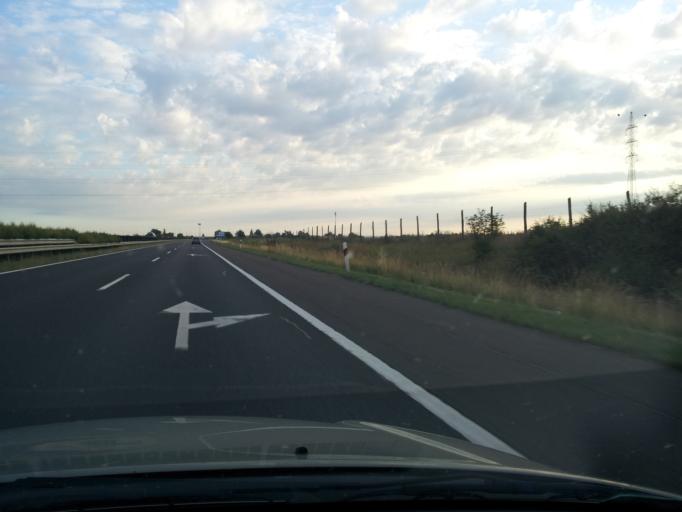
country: HU
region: Heves
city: Hered
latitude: 47.6719
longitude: 19.6349
